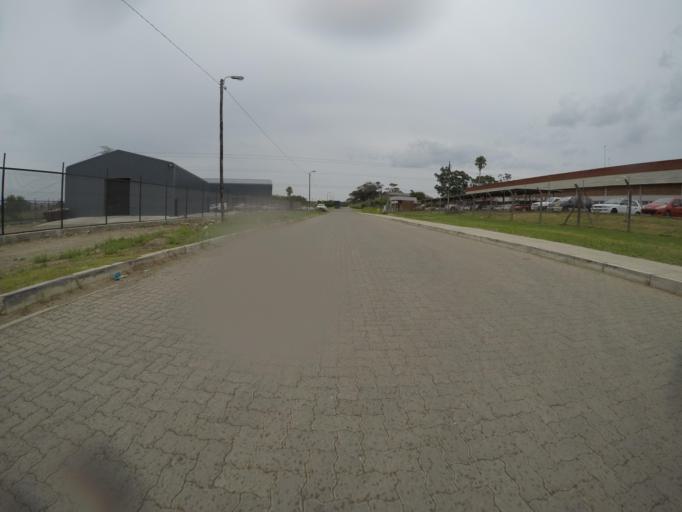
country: ZA
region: Eastern Cape
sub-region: Buffalo City Metropolitan Municipality
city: East London
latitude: -32.9906
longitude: 27.8301
